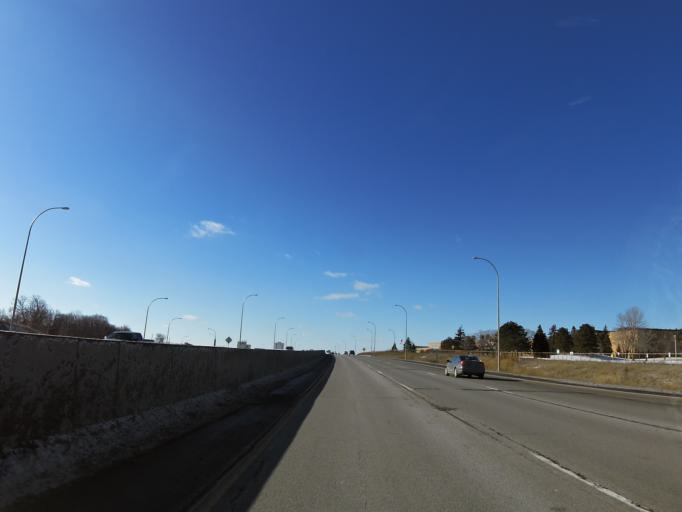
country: US
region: Minnesota
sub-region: Ramsey County
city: Maplewood
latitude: 44.9494
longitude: -92.9968
